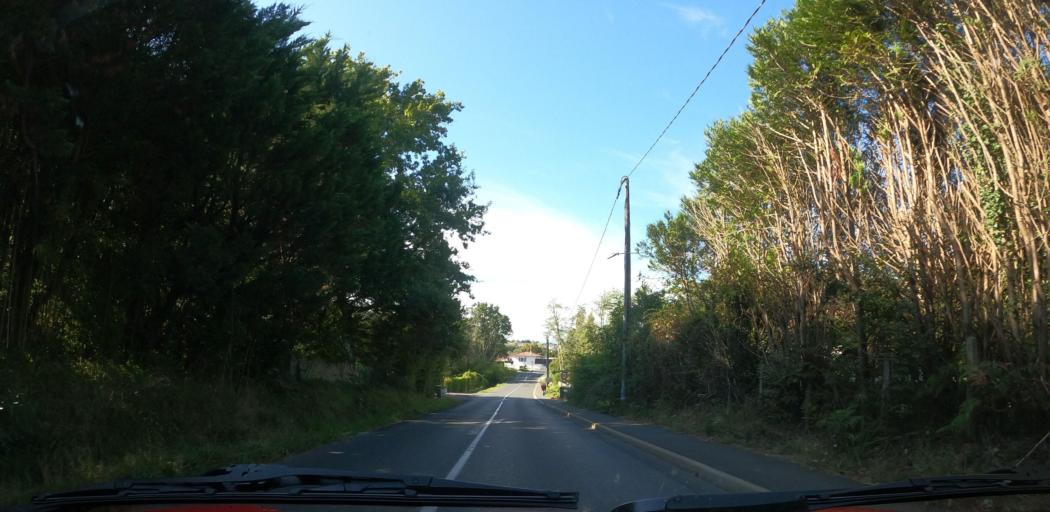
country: FR
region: Aquitaine
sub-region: Departement des Pyrenees-Atlantiques
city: Arbonne
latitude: 43.4409
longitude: -1.5467
